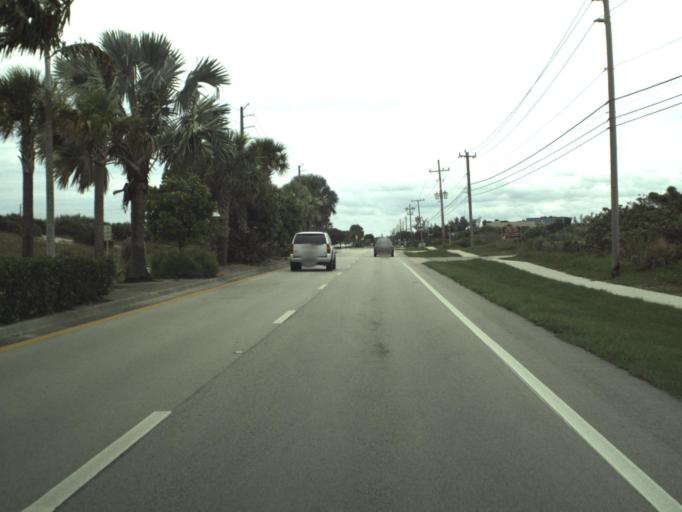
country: US
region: Florida
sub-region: Palm Beach County
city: Juno Beach
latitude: 26.8891
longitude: -80.0588
